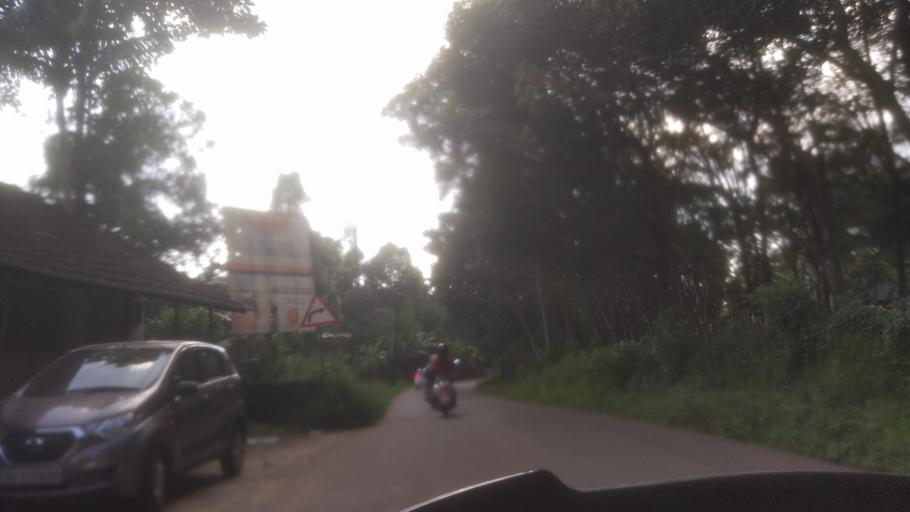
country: IN
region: Kerala
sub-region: Ernakulam
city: Muvattupula
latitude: 9.9958
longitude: 76.6124
